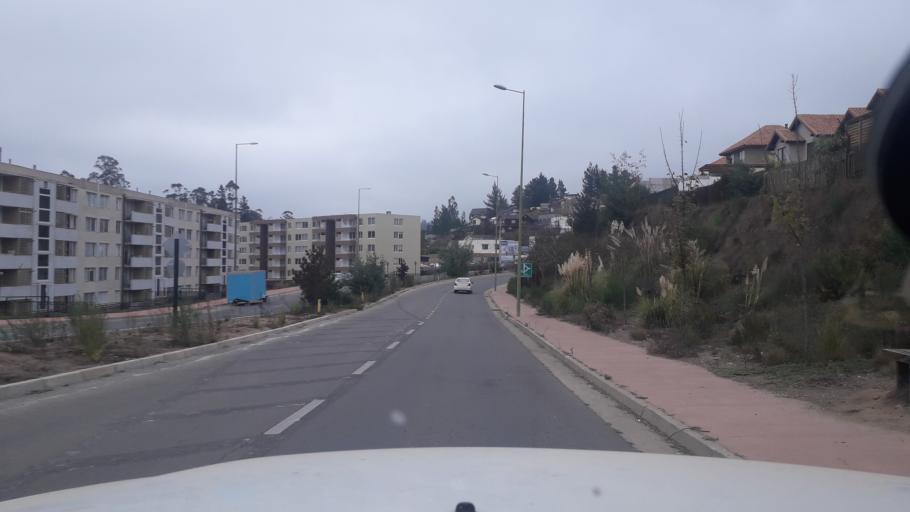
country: CL
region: Valparaiso
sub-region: Provincia de Valparaiso
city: Valparaiso
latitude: -33.1343
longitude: -71.5718
